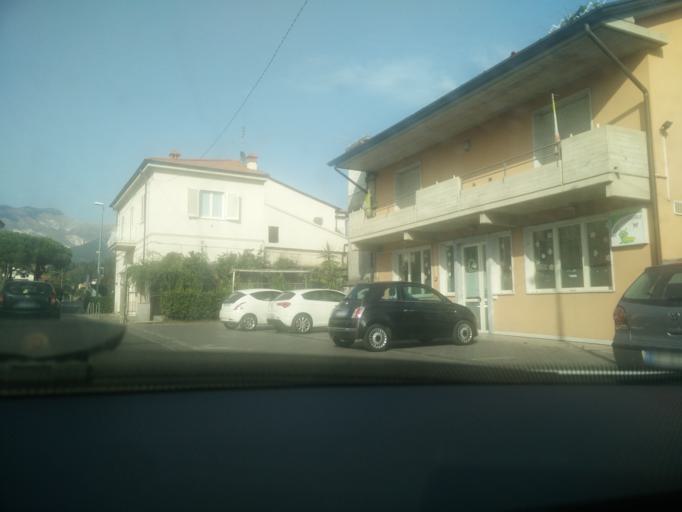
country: IT
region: Tuscany
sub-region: Provincia di Massa-Carrara
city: Carrara
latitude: 44.0520
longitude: 10.0711
